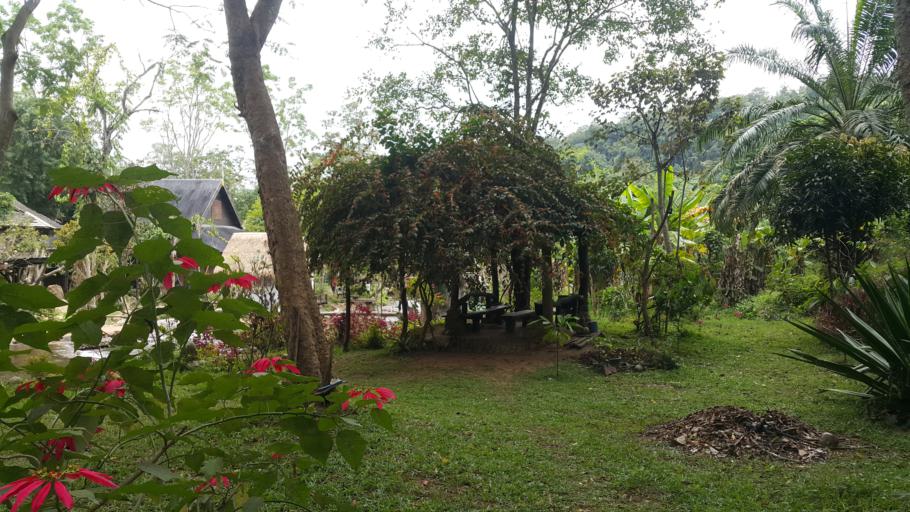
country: TH
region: Chiang Mai
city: Mae On
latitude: 18.8685
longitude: 99.3080
